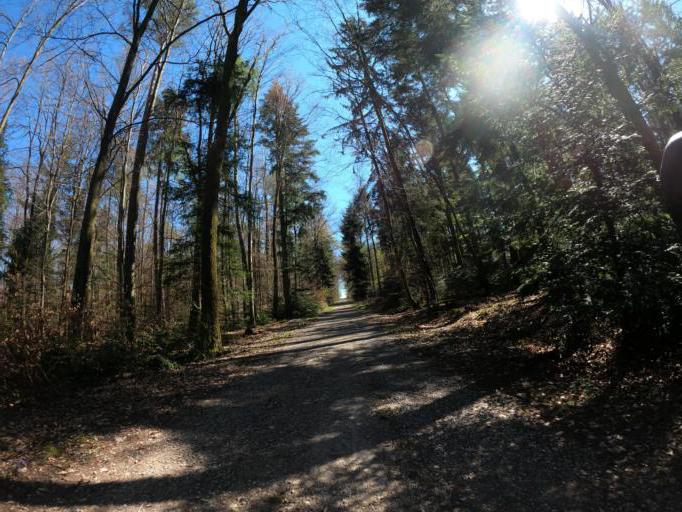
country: DE
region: Baden-Wuerttemberg
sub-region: Karlsruhe Region
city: Niefern-Oschelbronn
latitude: 48.8895
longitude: 8.7819
